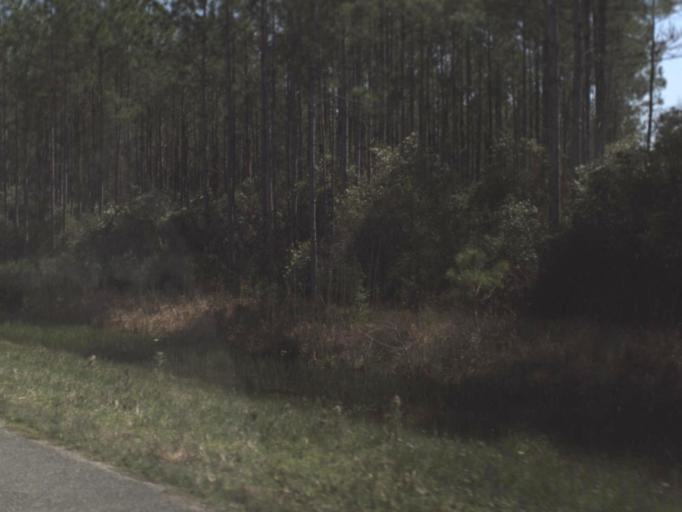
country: US
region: Florida
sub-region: Franklin County
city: Apalachicola
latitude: 29.7312
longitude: -85.1417
